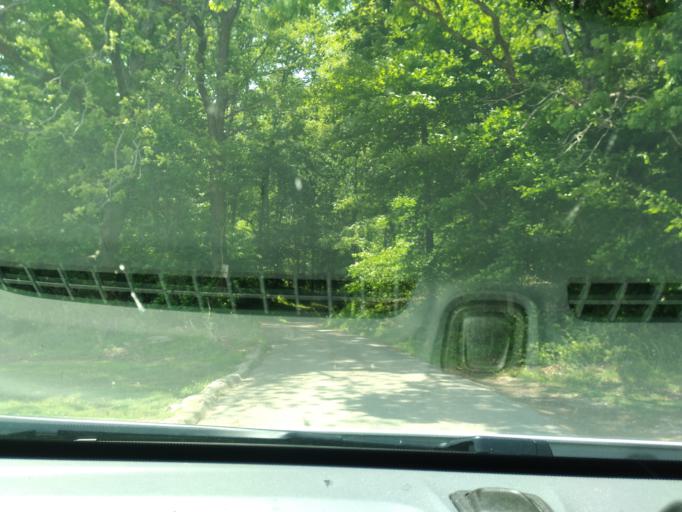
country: US
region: Maryland
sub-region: Prince George's County
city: Marlboro Meadows
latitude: 38.8512
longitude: -76.7005
